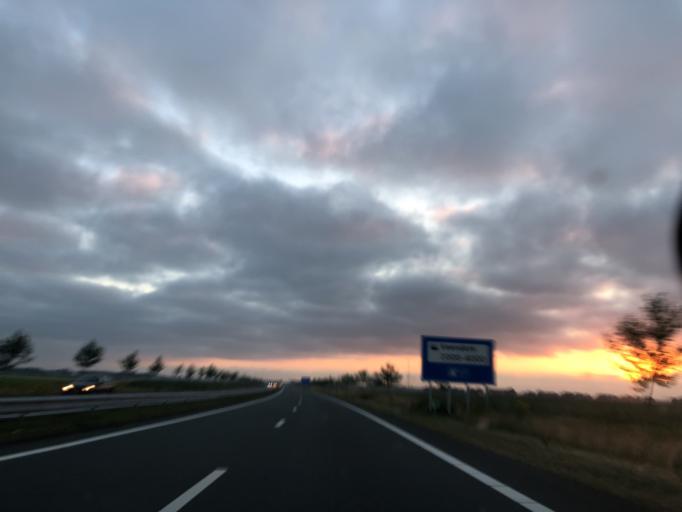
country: NL
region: Groningen
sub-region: Gemeente Veendam
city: Veendam
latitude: 53.0648
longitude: 6.8742
